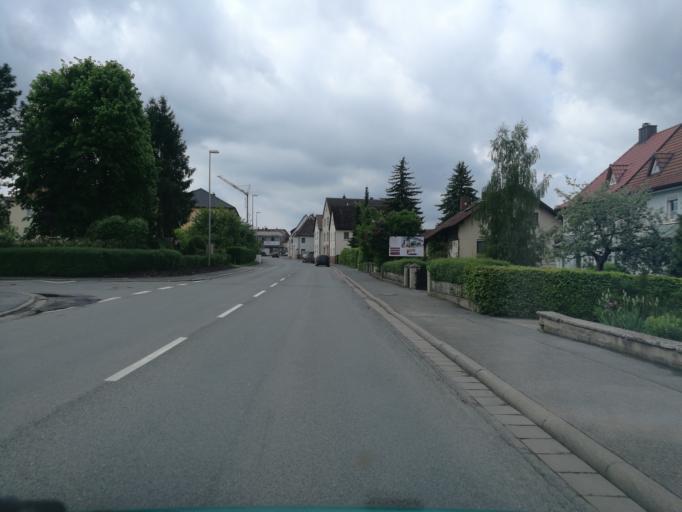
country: DE
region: Bavaria
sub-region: Upper Franconia
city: Bad Staffelstein
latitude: 50.1036
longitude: 11.0049
